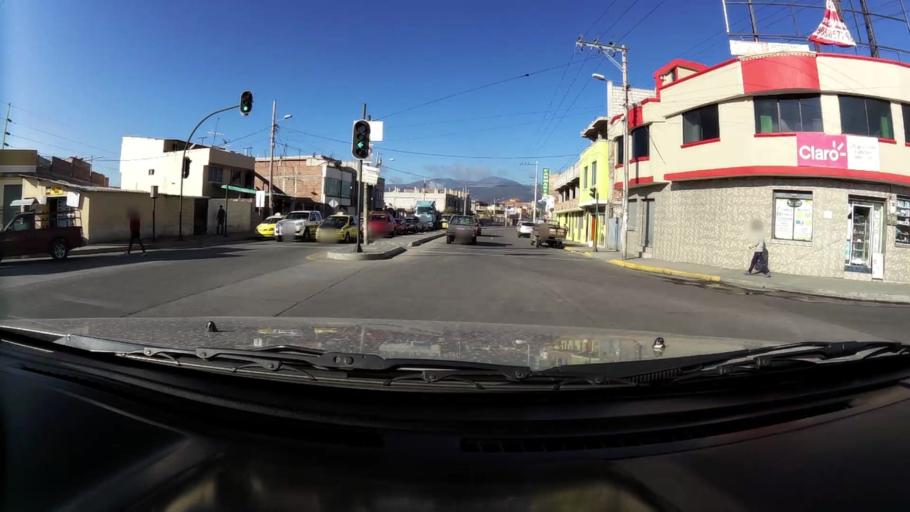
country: EC
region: Chimborazo
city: Riobamba
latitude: -1.6895
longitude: -78.6320
